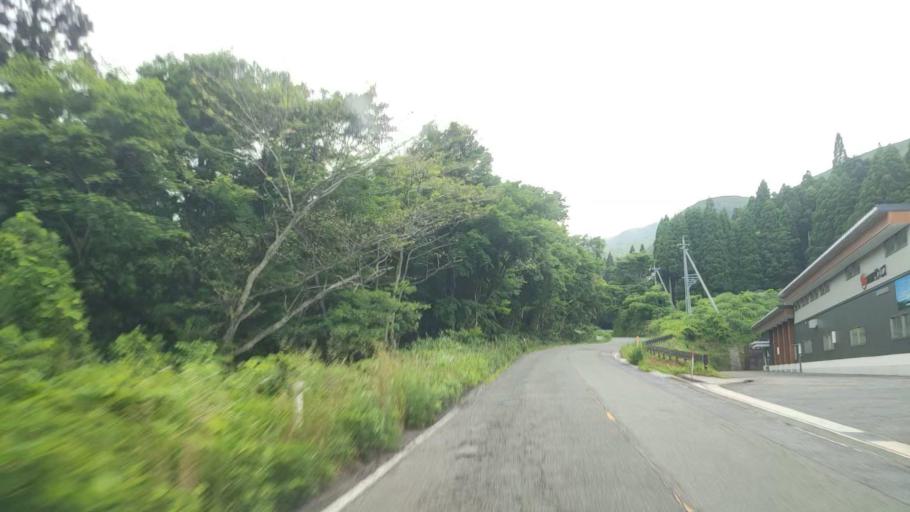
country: JP
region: Tottori
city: Yonago
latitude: 35.3273
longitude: 133.5570
